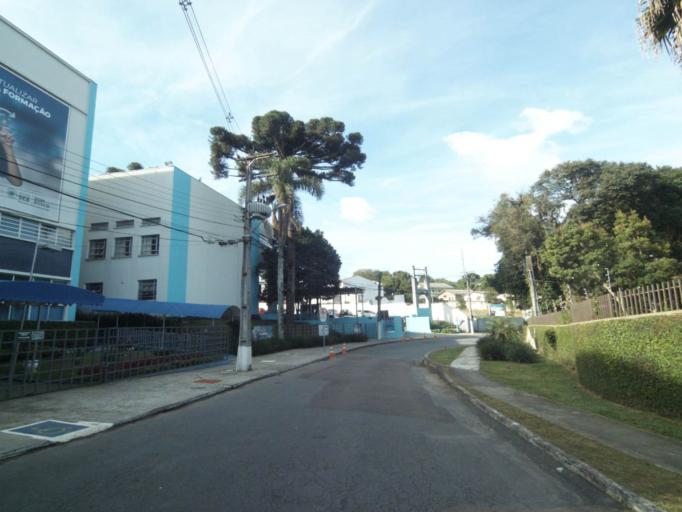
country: BR
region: Parana
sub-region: Curitiba
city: Curitiba
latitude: -25.4178
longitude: -49.2965
